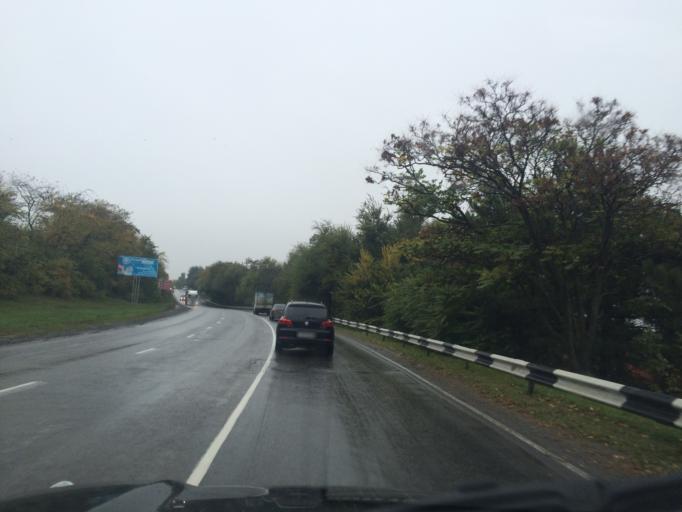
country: RU
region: Rostov
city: Azov
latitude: 47.0869
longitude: 39.4692
